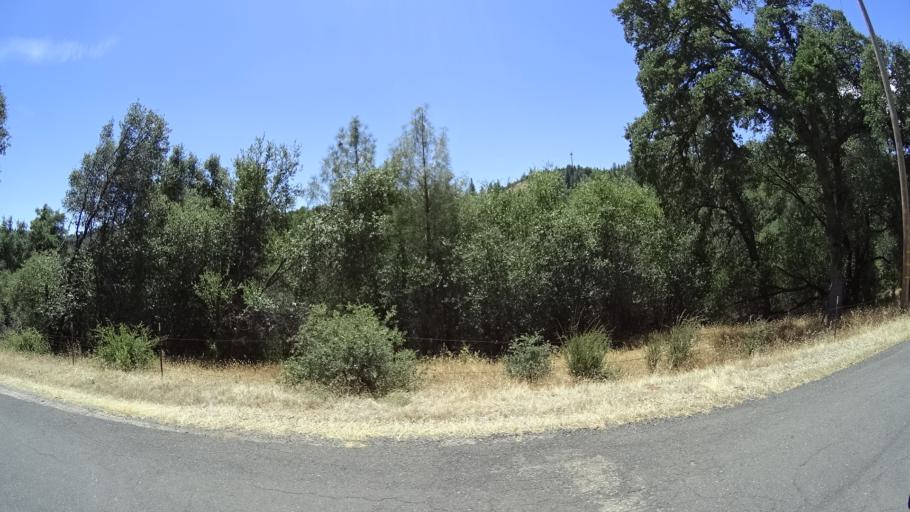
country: US
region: California
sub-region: Calaveras County
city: Forest Meadows
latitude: 38.2085
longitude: -120.4588
